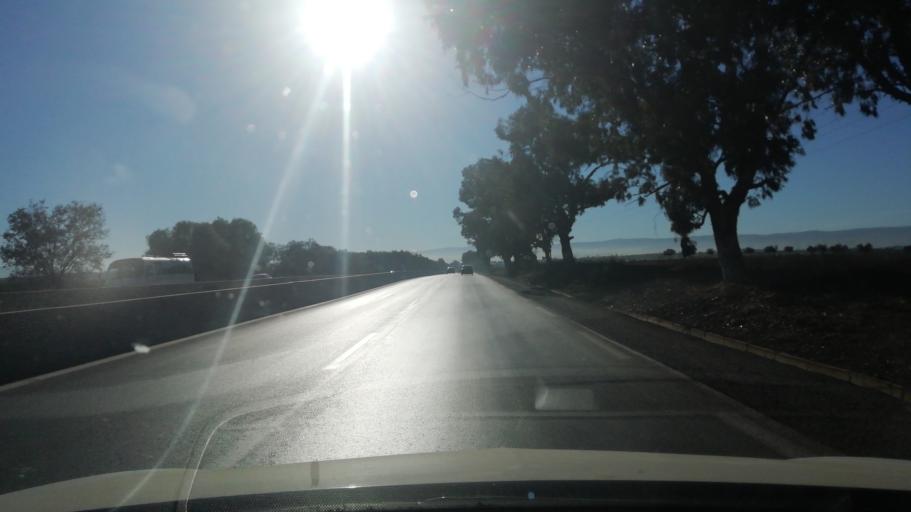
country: DZ
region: Tlemcen
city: Remchi
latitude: 35.0128
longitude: -1.3923
